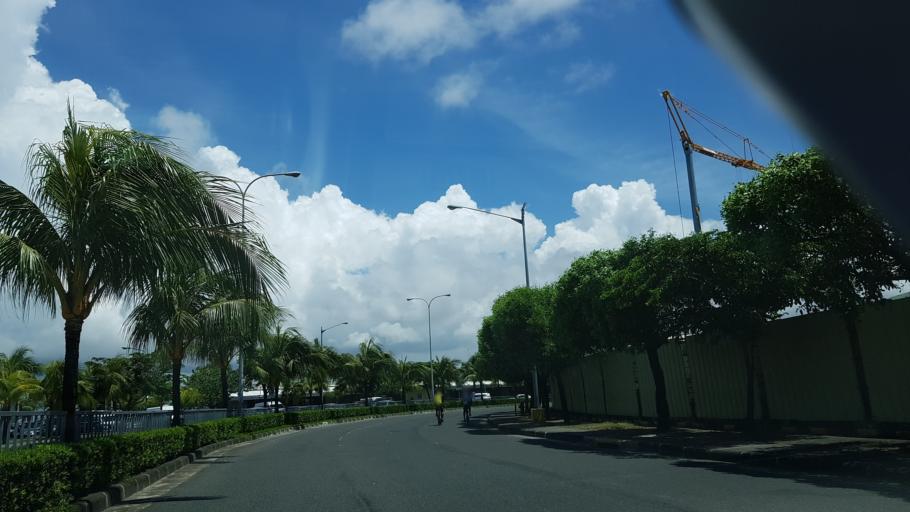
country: PH
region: Metro Manila
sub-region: City of Manila
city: Port Area
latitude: 14.5401
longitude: 120.9796
